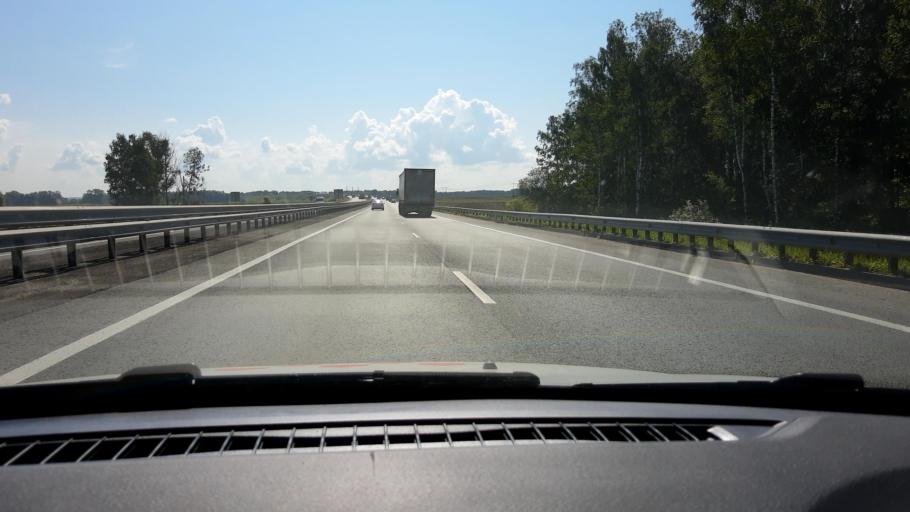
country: RU
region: Nizjnij Novgorod
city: Burevestnik
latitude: 56.1204
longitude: 43.8128
